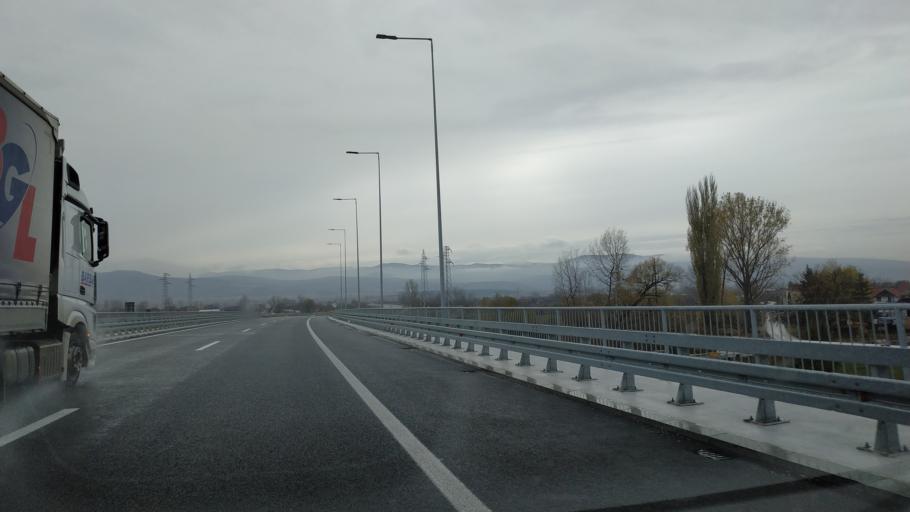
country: RS
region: Central Serbia
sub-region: Pirotski Okrug
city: Pirot
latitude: 43.1591
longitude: 22.5740
